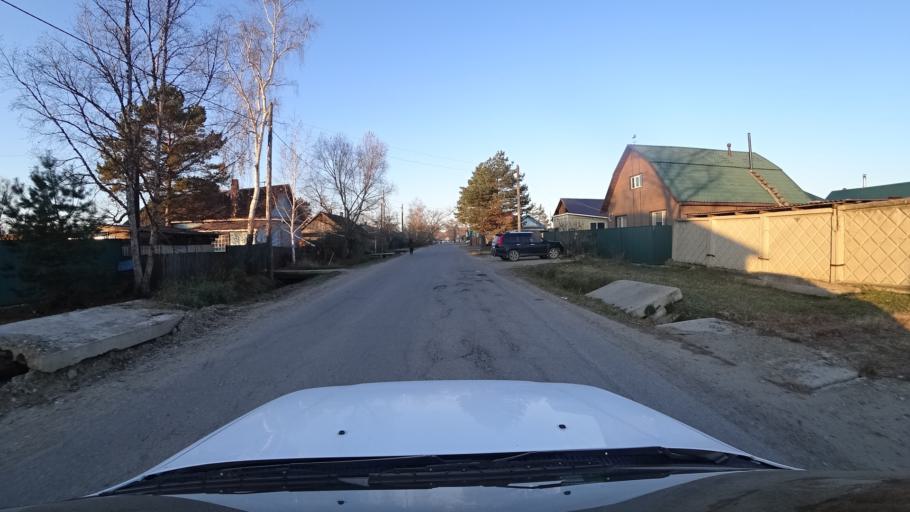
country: RU
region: Primorskiy
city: Dal'nerechensk
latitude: 45.9260
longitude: 133.7345
